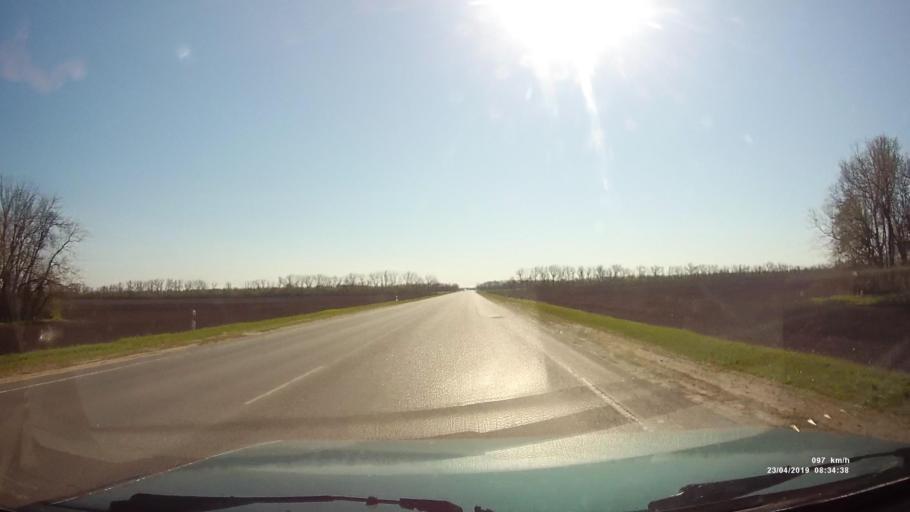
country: RU
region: Rostov
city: Tselina
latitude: 46.5236
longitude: 41.1169
